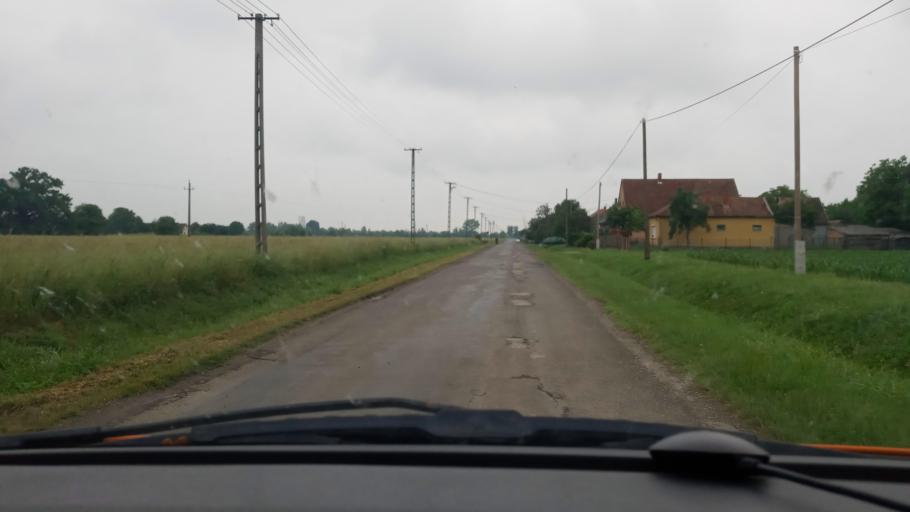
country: HU
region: Baranya
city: Szentlorinc
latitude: 46.0495
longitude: 17.9681
